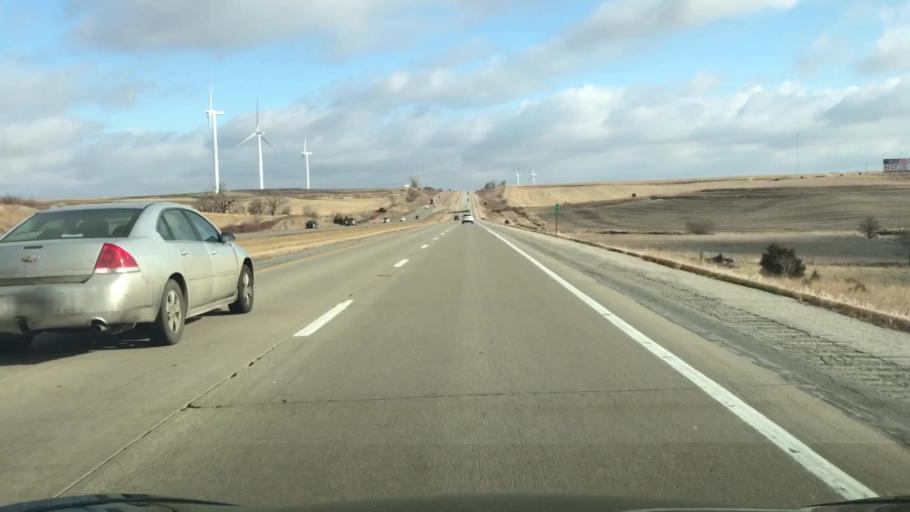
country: US
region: Iowa
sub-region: Guthrie County
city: Guthrie Center
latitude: 41.4961
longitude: -94.7074
